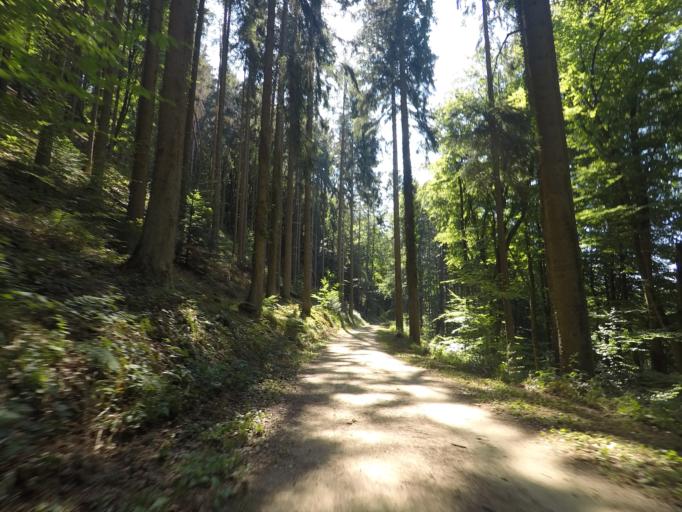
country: LU
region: Luxembourg
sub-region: Canton de Capellen
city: Kopstal
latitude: 49.6467
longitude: 6.0561
